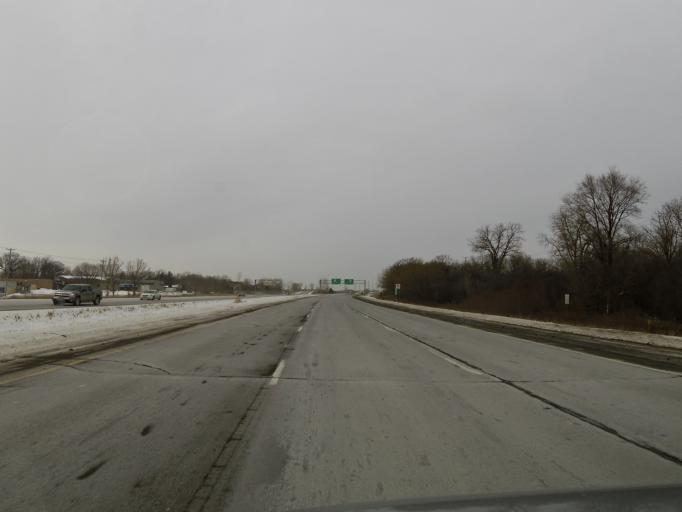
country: US
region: Minnesota
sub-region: Scott County
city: Savage
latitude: 44.7813
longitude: -93.3885
